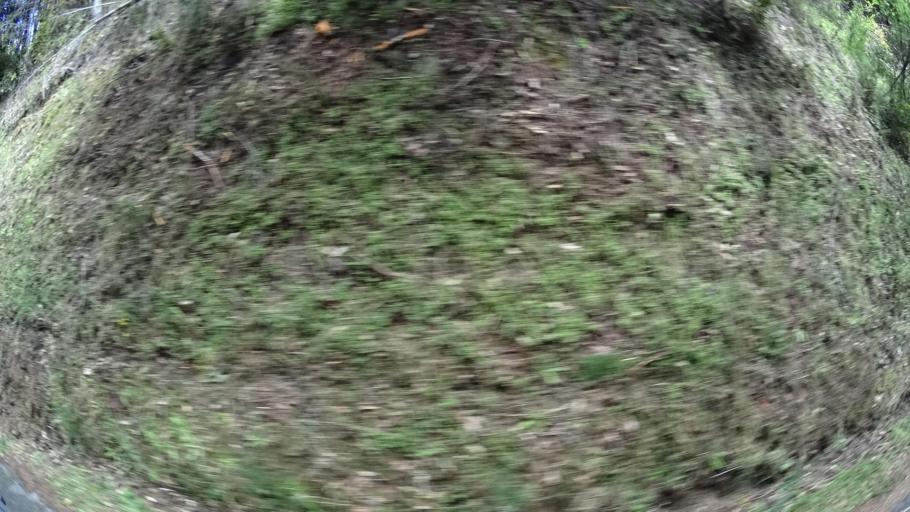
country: US
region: California
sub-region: Humboldt County
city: Blue Lake
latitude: 40.7617
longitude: -123.9206
